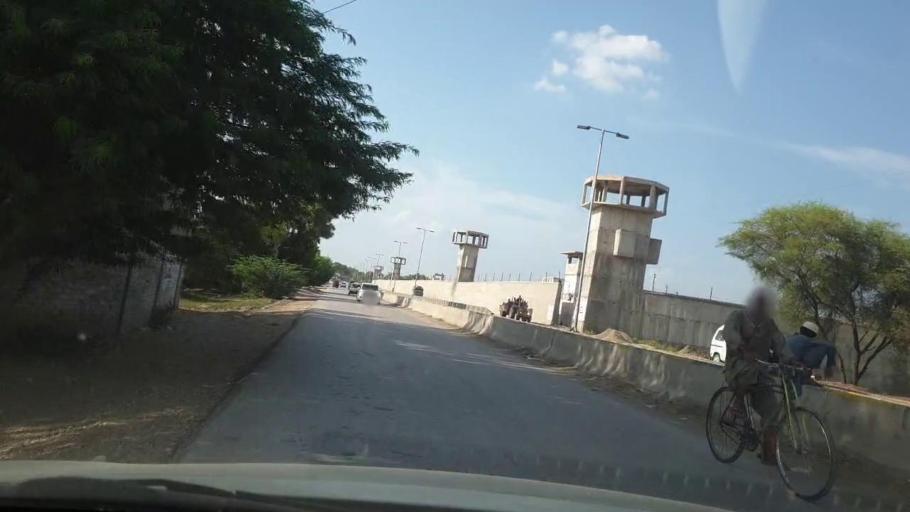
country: PK
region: Sindh
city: Sukkur
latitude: 27.6643
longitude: 68.8467
